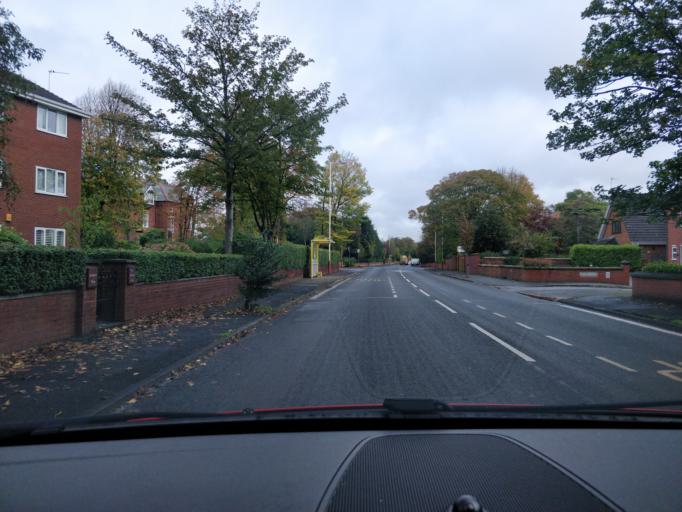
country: GB
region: England
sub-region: Sefton
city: Southport
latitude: 53.6341
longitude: -3.0236
